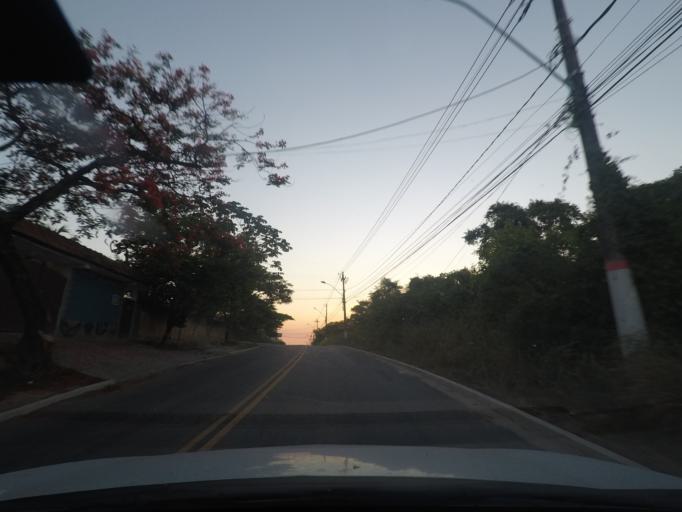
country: BR
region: Rio de Janeiro
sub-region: Sao Goncalo
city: Sao Goncalo
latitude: -22.9490
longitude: -42.9701
